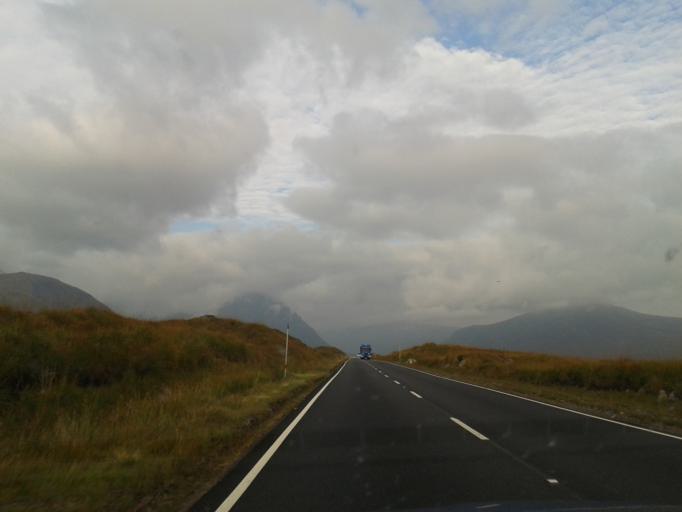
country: GB
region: Scotland
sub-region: Highland
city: Spean Bridge
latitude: 56.6301
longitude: -4.7805
